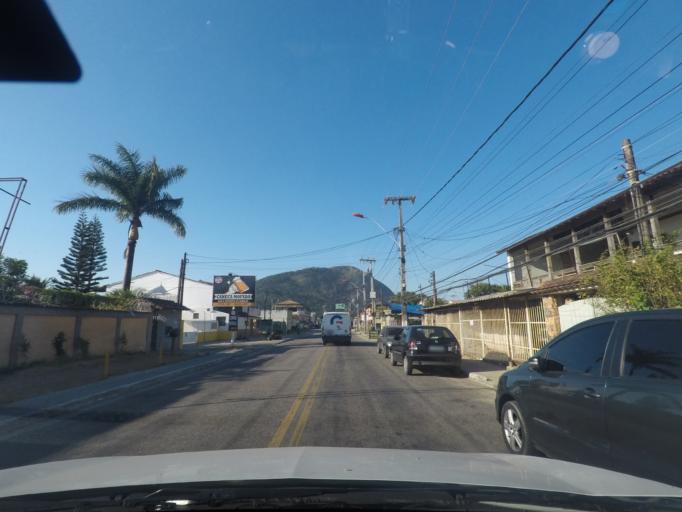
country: BR
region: Rio de Janeiro
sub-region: Marica
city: Marica
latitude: -22.9577
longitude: -42.9622
